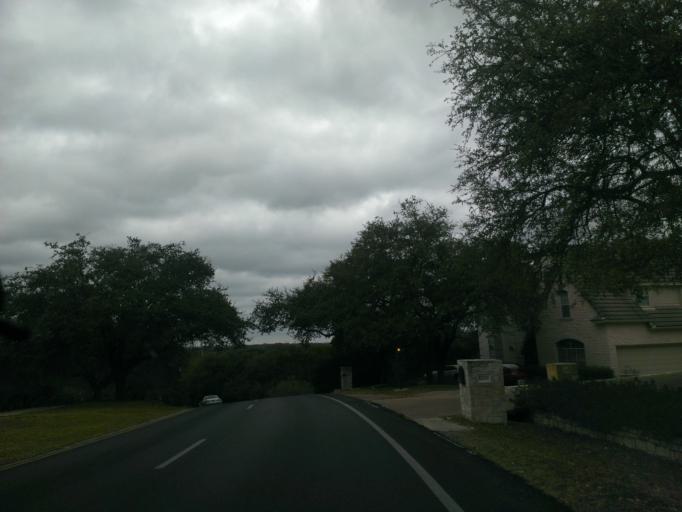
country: US
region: Texas
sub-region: Travis County
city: Lakeway
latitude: 30.3571
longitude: -97.9655
